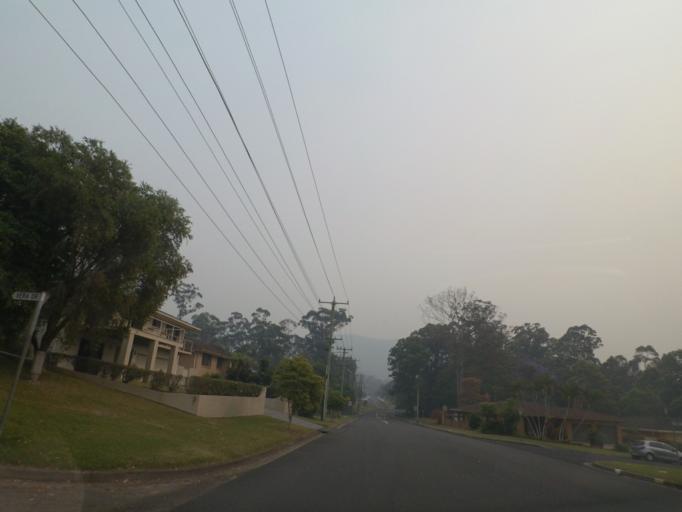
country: AU
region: New South Wales
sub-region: Coffs Harbour
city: Coffs Harbour
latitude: -30.2810
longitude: 153.1035
